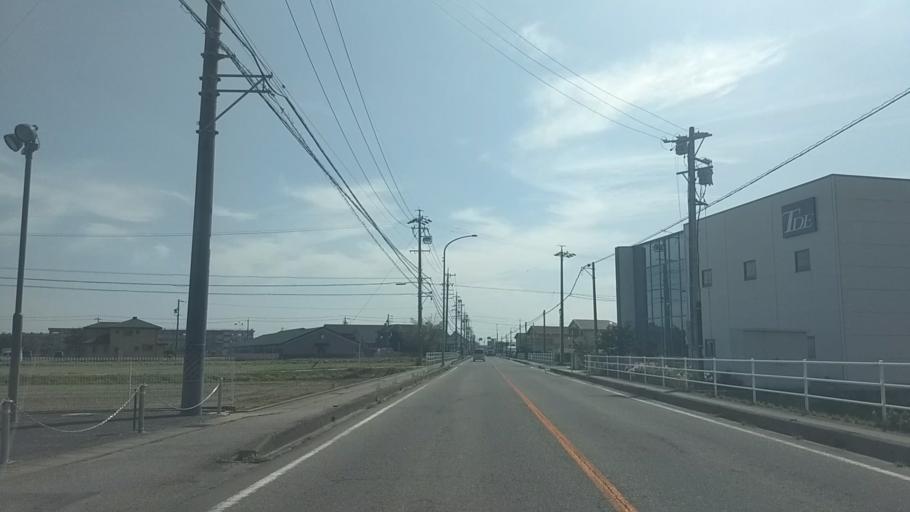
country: JP
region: Aichi
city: Anjo
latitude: 34.9698
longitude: 137.1049
